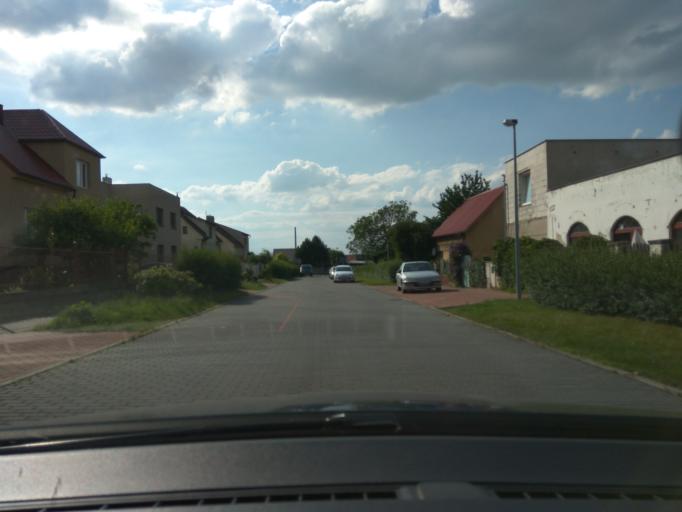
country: CZ
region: Praha
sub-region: Praha 19
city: Kbely
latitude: 50.1544
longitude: 14.5397
